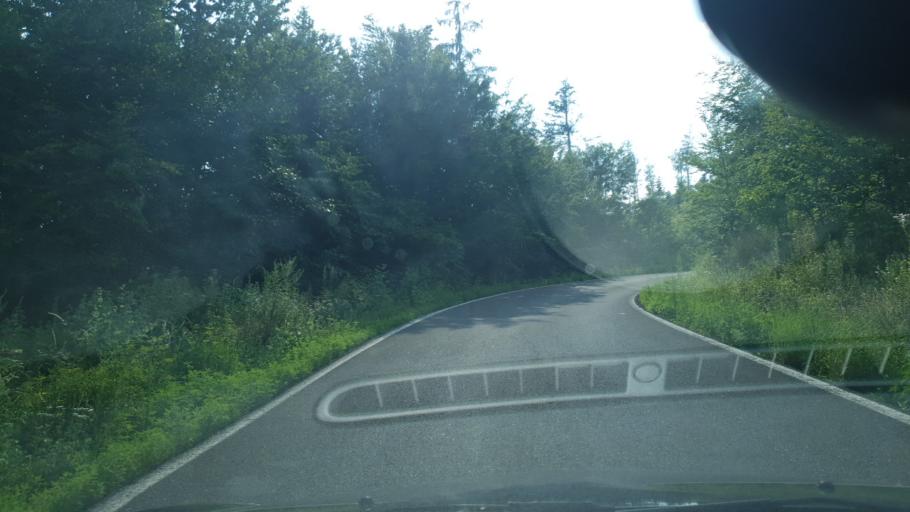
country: HR
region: Grad Zagreb
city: Kasina
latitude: 45.8906
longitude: 15.9609
